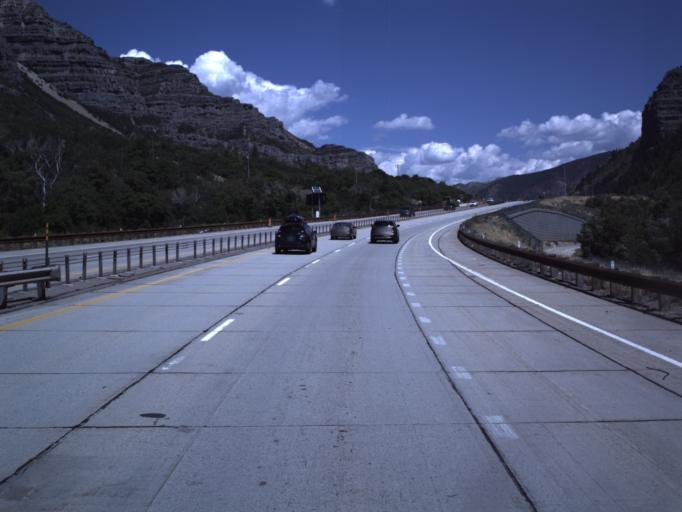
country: US
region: Utah
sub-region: Utah County
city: Orem
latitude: 40.3390
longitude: -111.6090
